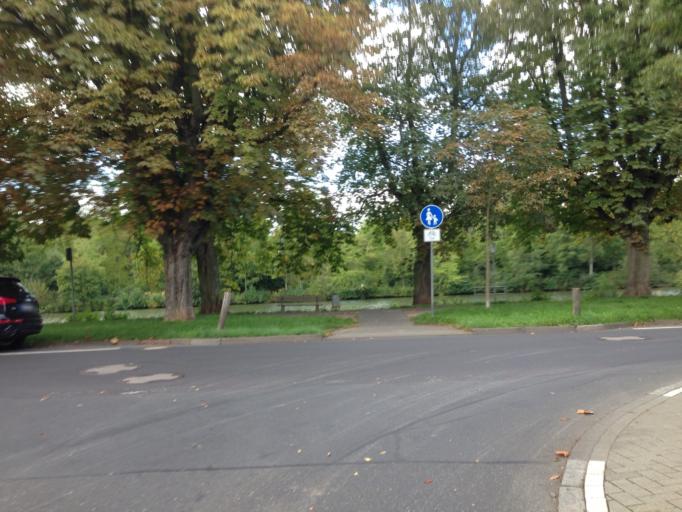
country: DE
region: Hesse
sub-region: Regierungsbezirk Giessen
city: Giessen
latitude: 50.5895
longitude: 8.6900
